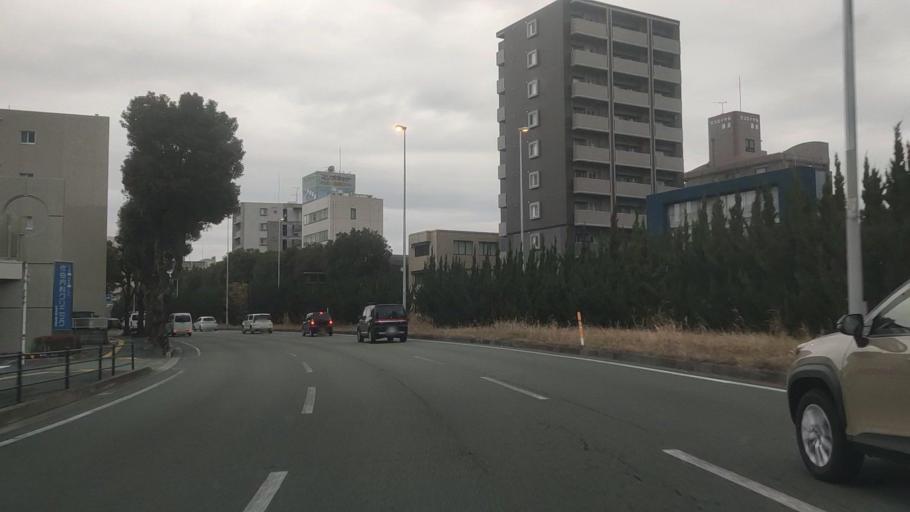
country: JP
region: Kumamoto
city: Kumamoto
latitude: 32.7853
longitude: 130.7467
